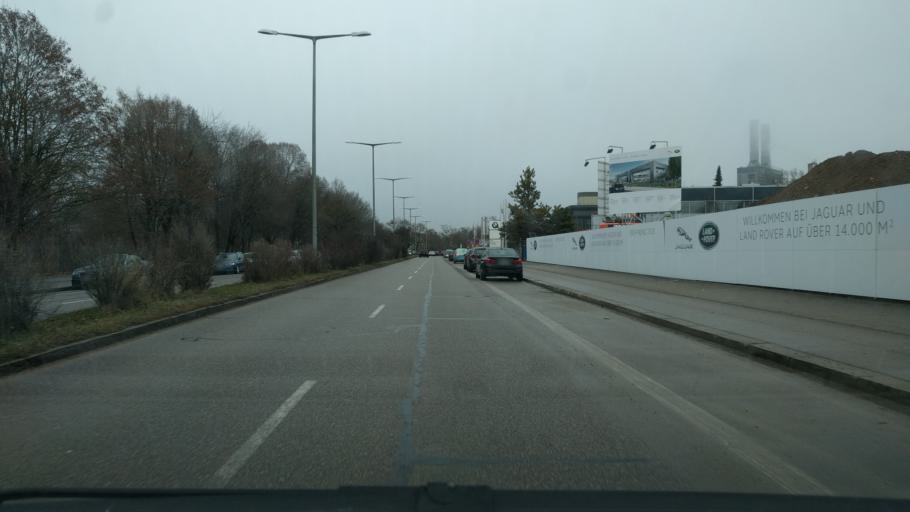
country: DE
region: Bavaria
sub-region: Upper Bavaria
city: Pullach im Isartal
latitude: 48.0908
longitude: 11.5029
